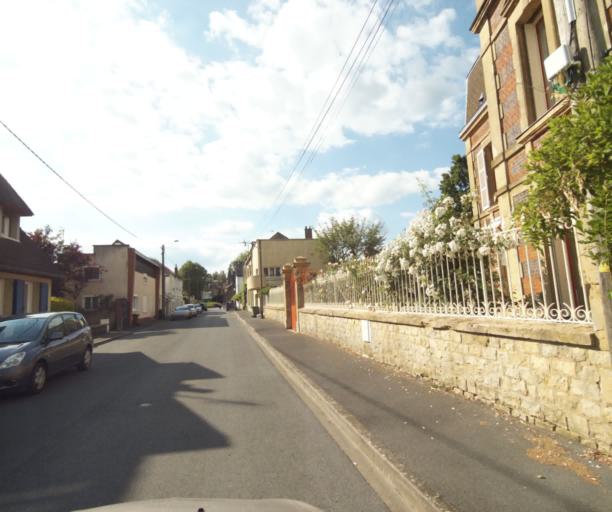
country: FR
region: Champagne-Ardenne
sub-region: Departement des Ardennes
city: Montcy-Notre-Dame
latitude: 49.7745
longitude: 4.7336
